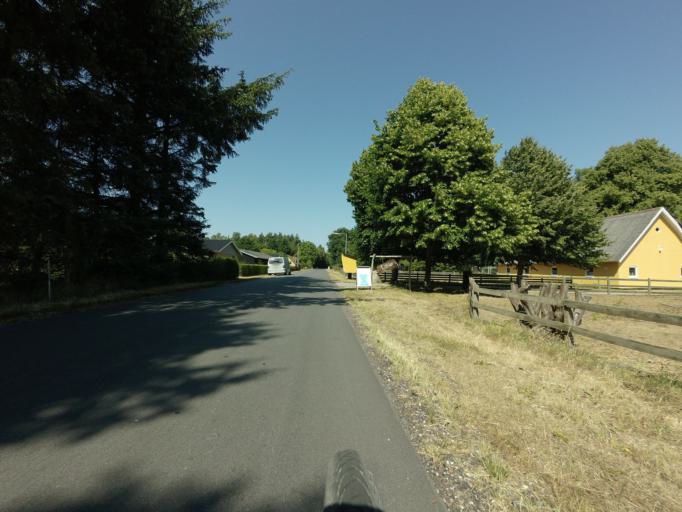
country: DK
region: North Denmark
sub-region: Laeso Kommune
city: Byrum
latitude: 57.2606
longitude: 11.0001
